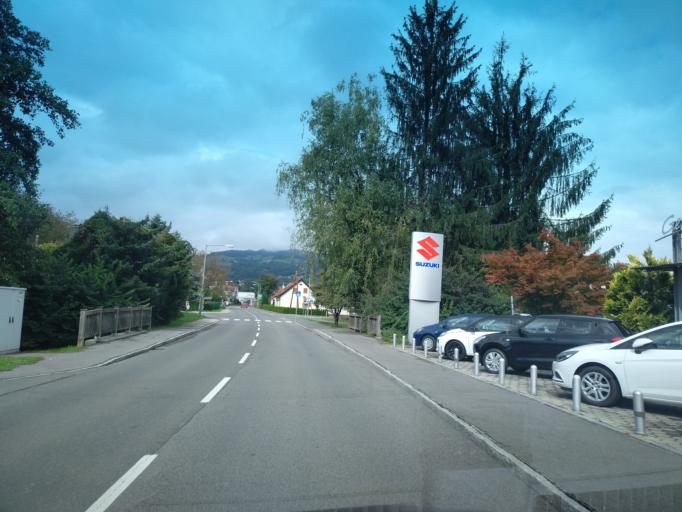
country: AT
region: Styria
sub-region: Politischer Bezirk Deutschlandsberg
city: Deutschlandsberg
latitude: 46.8128
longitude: 15.2252
